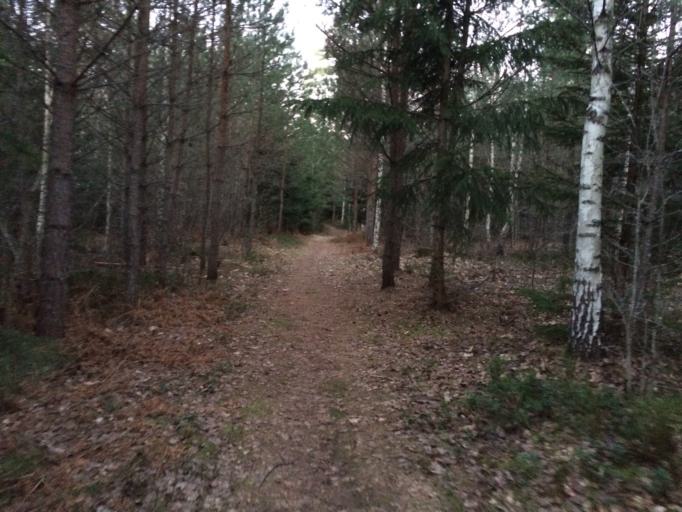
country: SE
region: Vaestmanland
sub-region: Hallstahammars Kommun
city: Hallstahammar
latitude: 59.6166
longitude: 16.1985
